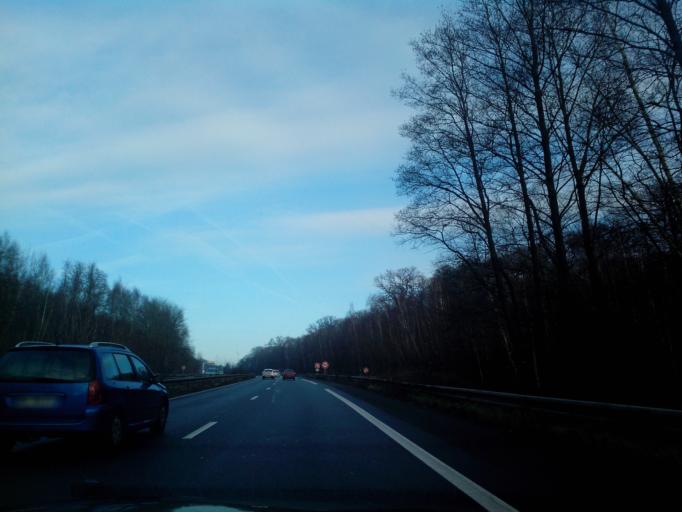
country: FR
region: Ile-de-France
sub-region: Departement du Val-d'Oise
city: L'Isle-Adam
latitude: 49.0849
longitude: 2.2571
